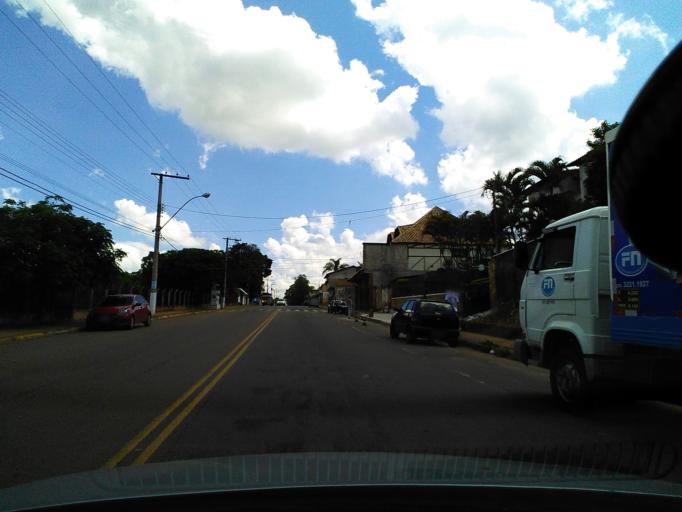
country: BR
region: Minas Gerais
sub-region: Tres Coracoes
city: Tres Coracoes
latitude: -21.7220
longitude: -45.2625
